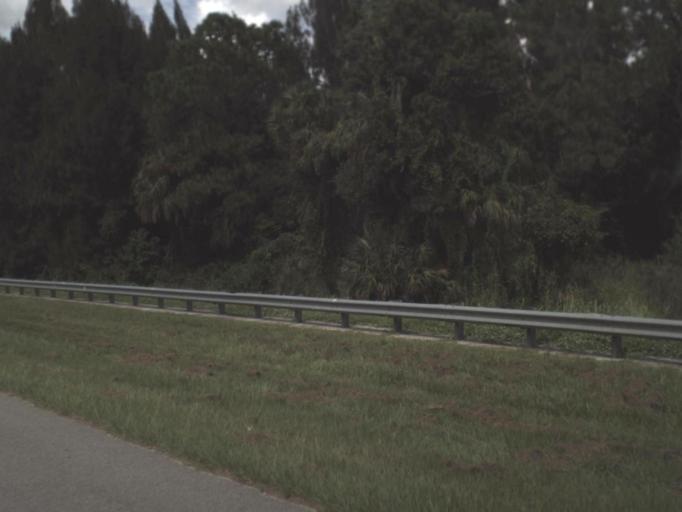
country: US
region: Florida
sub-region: Collier County
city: Immokalee
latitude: 26.4078
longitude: -81.3968
